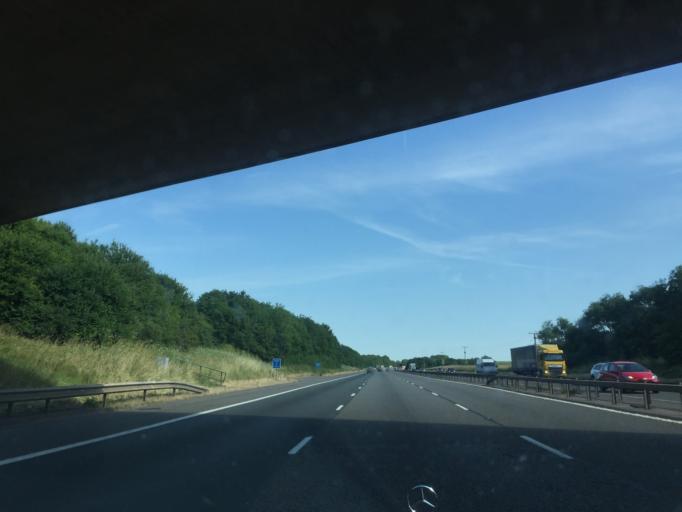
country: GB
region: England
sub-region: Warwickshire
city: Harbury
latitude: 52.1650
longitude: -1.4362
